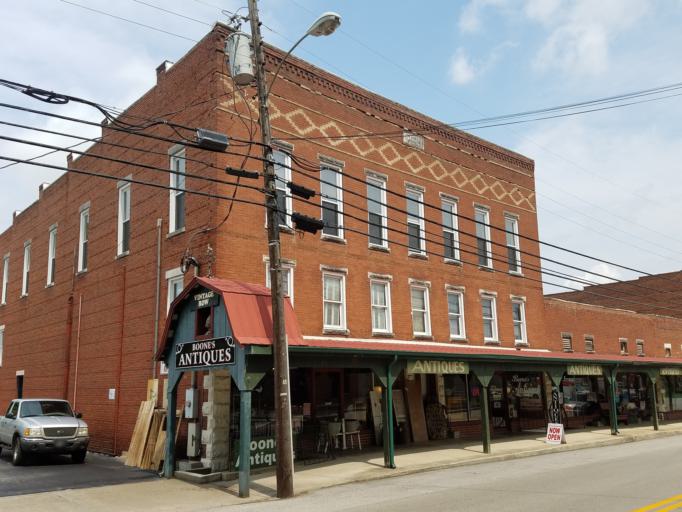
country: US
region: Kentucky
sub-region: Edmonson County
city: Brownsville
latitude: 37.0532
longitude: -86.2081
